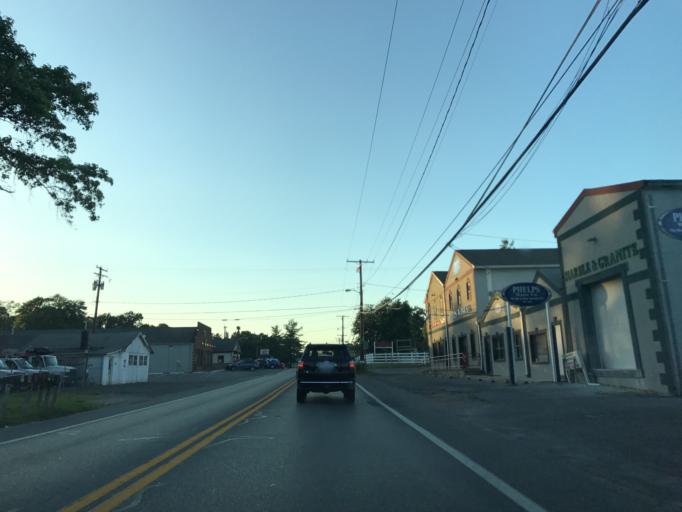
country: US
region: Maryland
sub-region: Anne Arundel County
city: Londontowne
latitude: 38.9316
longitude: -76.5567
